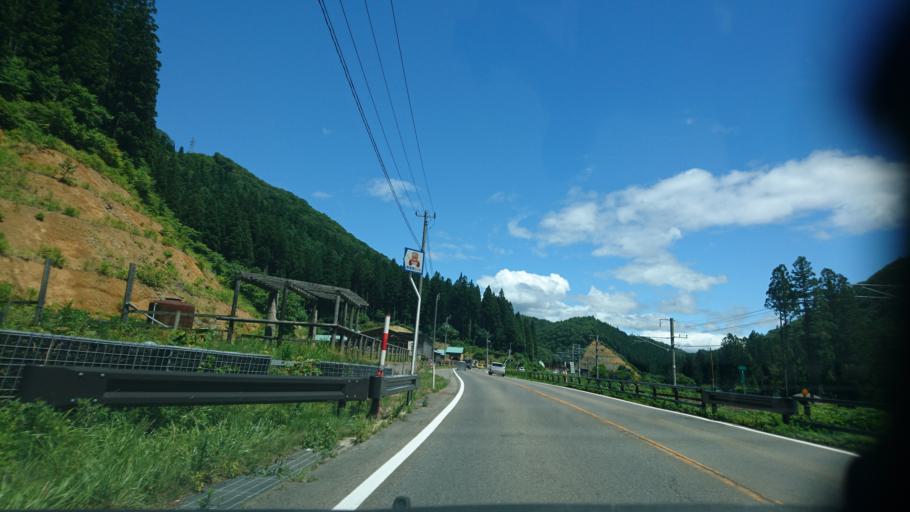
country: JP
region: Akita
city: Kakunodatemachi
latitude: 39.6460
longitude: 140.6644
